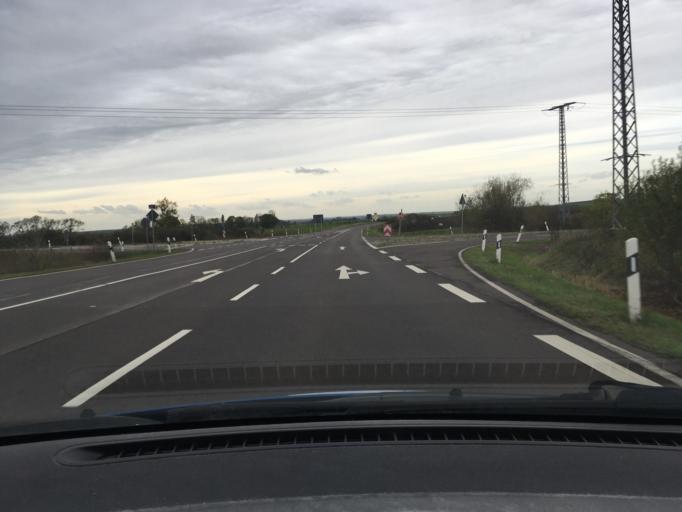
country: DE
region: Saxony-Anhalt
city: Leitzkau
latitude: 52.0496
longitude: 11.9503
